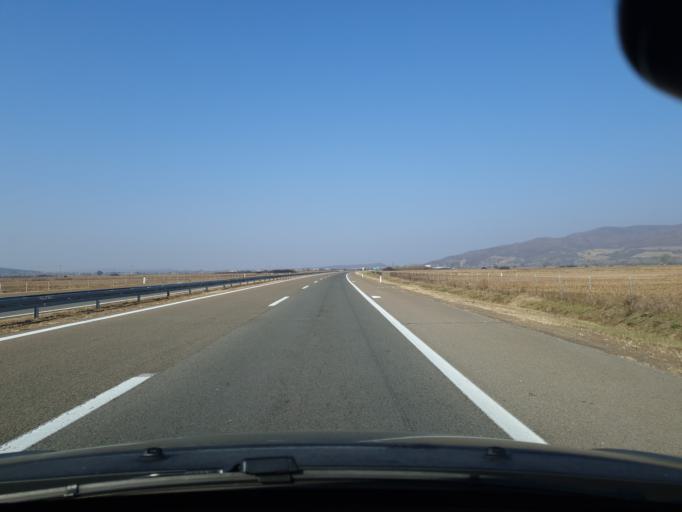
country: RS
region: Central Serbia
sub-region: Nisavski Okrug
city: Doljevac
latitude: 43.1758
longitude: 21.8670
